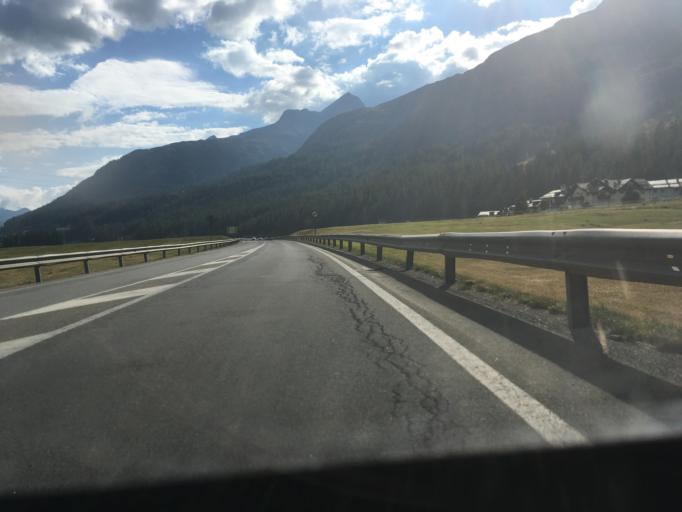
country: CH
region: Grisons
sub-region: Maloja District
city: Silvaplana
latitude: 46.4758
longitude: 9.8142
